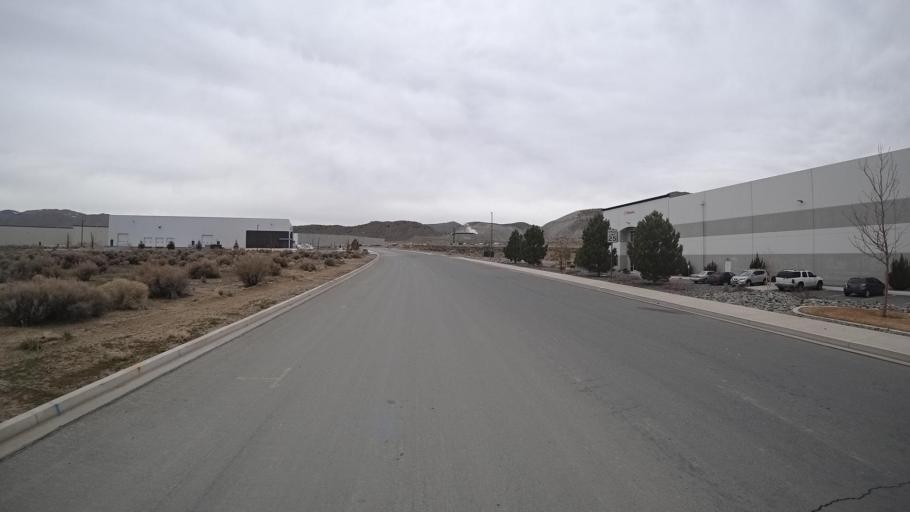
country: US
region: Nevada
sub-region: Washoe County
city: Spanish Springs
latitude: 39.6769
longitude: -119.7154
